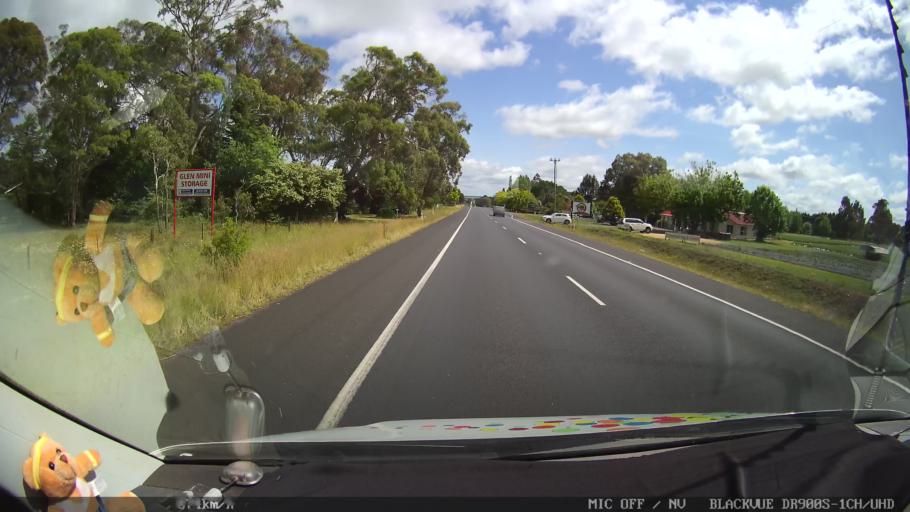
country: AU
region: New South Wales
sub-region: Glen Innes Severn
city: Glen Innes
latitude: -29.7621
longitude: 151.7337
